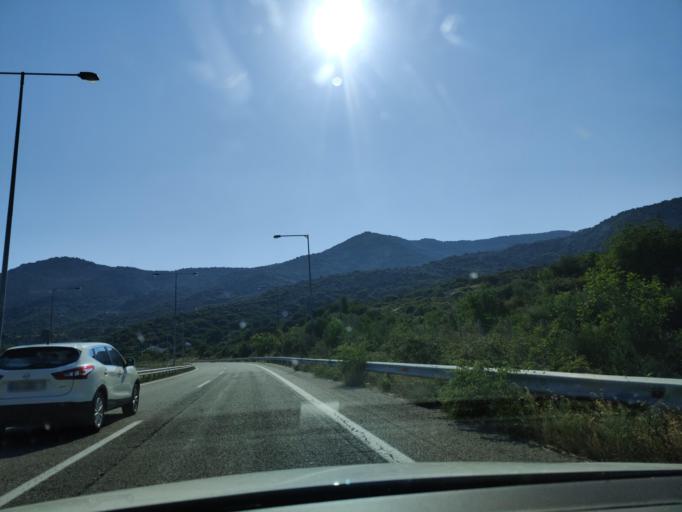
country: GR
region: East Macedonia and Thrace
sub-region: Nomos Kavalas
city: Palaio Tsifliki
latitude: 40.9023
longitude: 24.3346
